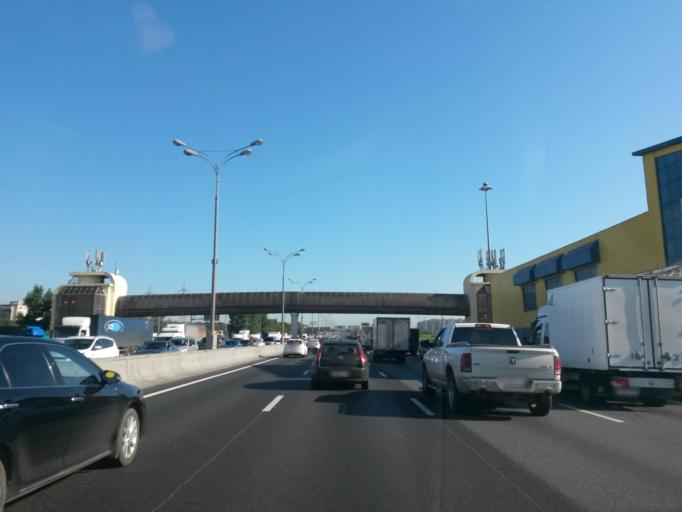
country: RU
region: Moskovskaya
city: Kuskovo
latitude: 55.7317
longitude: 37.8407
